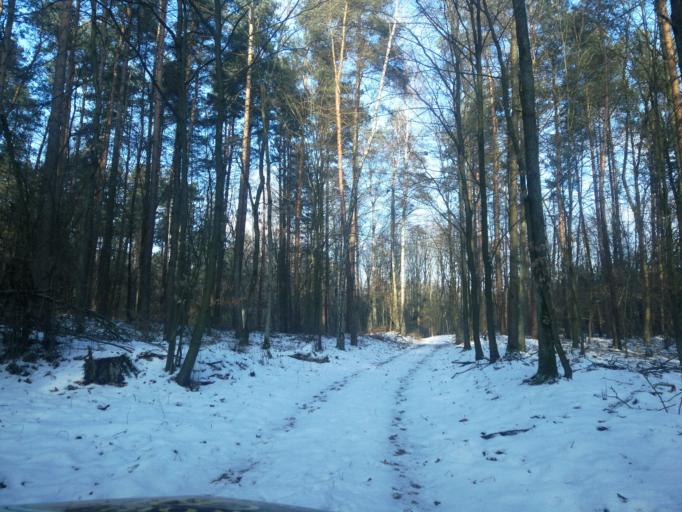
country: PL
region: Kujawsko-Pomorskie
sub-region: Powiat brodnicki
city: Gorzno
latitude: 53.2178
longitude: 19.6480
